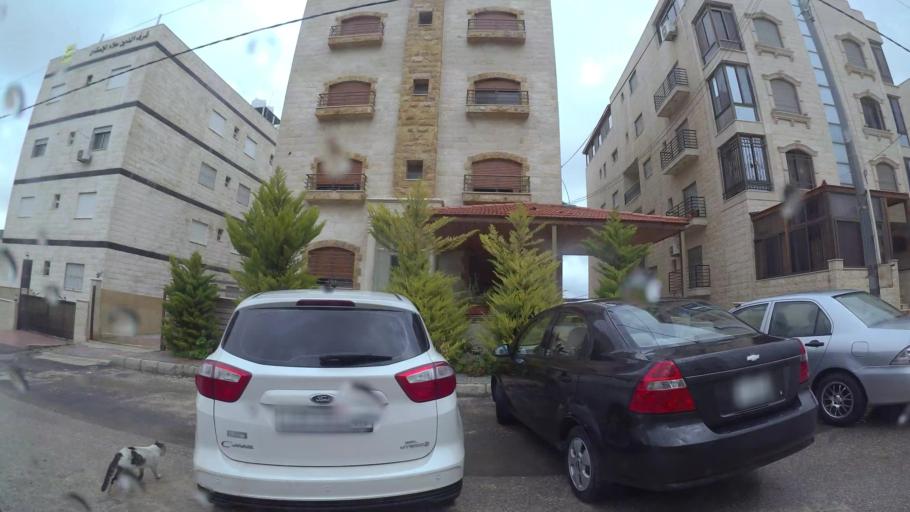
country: JO
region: Amman
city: Al Jubayhah
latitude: 32.0356
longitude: 35.8859
